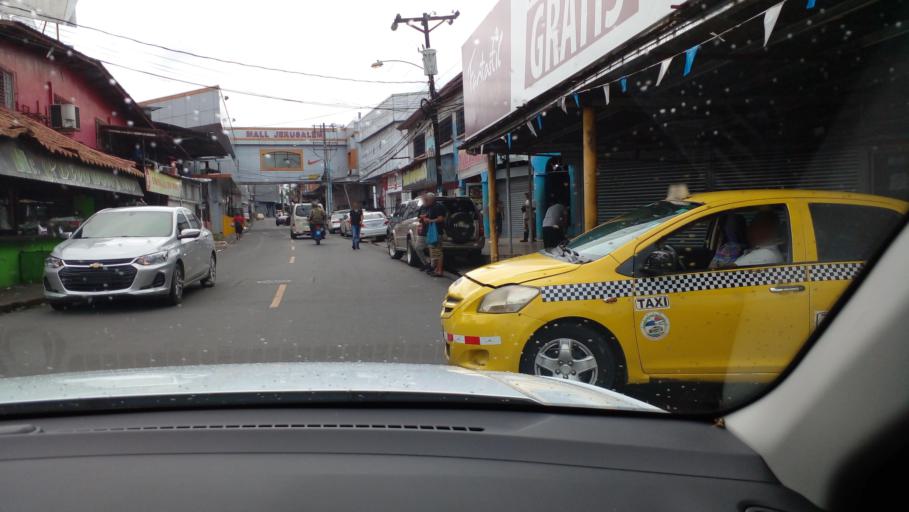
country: CR
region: Puntarenas
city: Canoas
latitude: 8.5338
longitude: -82.8379
